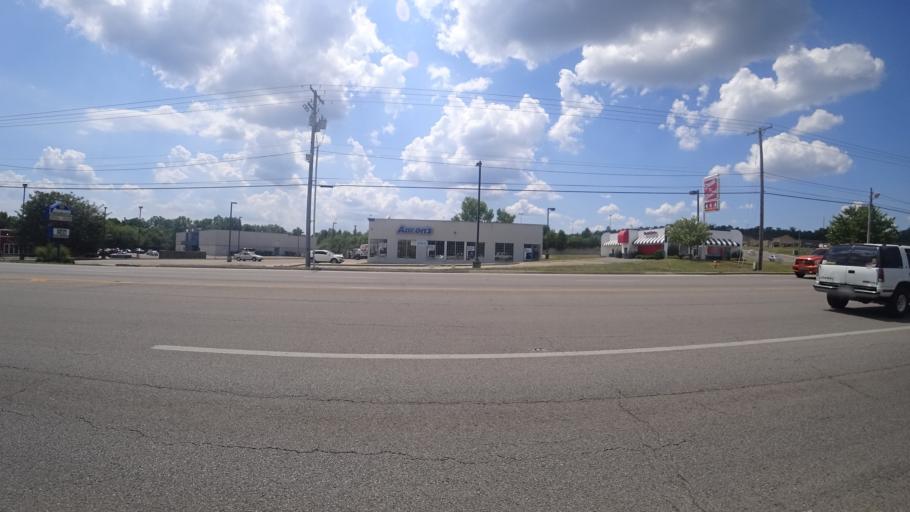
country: US
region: Ohio
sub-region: Butler County
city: Hamilton
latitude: 39.4253
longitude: -84.5958
